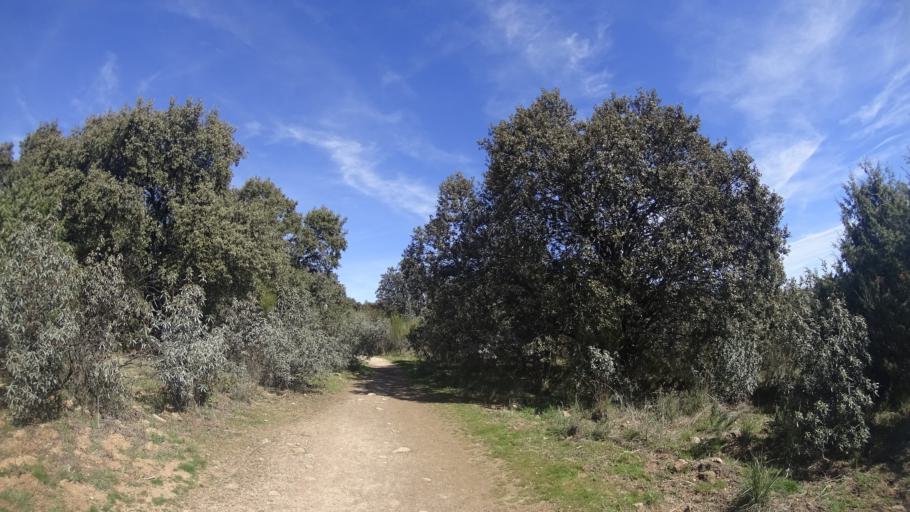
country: ES
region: Madrid
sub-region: Provincia de Madrid
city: Galapagar
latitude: 40.5876
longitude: -3.9851
